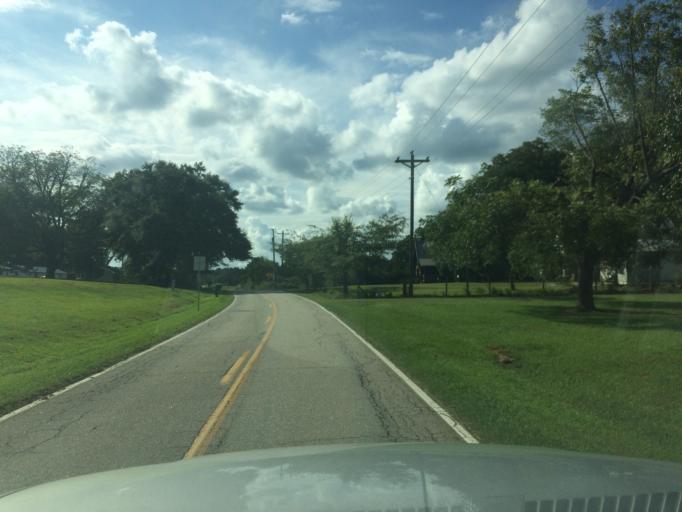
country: US
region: South Carolina
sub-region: Spartanburg County
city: Woodruff
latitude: 34.7698
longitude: -82.1087
